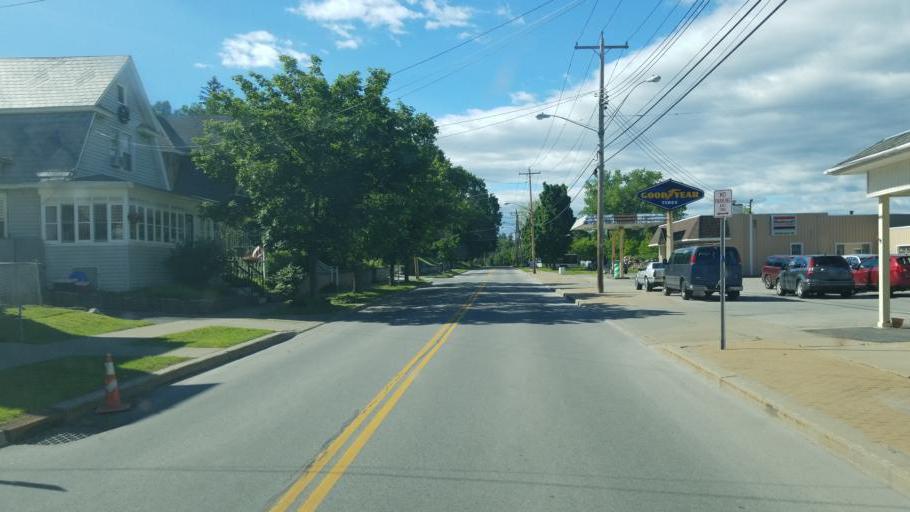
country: US
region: New York
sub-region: Montgomery County
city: Fort Plain
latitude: 42.9346
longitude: -74.6254
